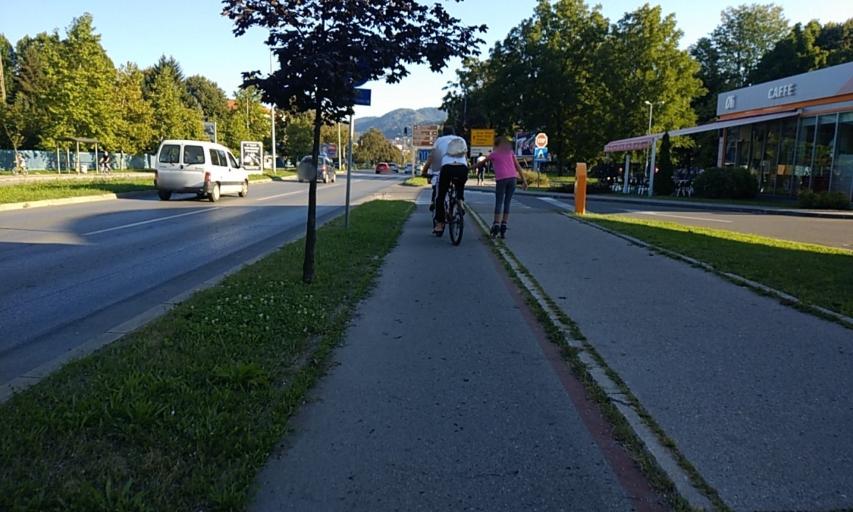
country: BA
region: Republika Srpska
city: Starcevica
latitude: 44.7756
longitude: 17.2070
